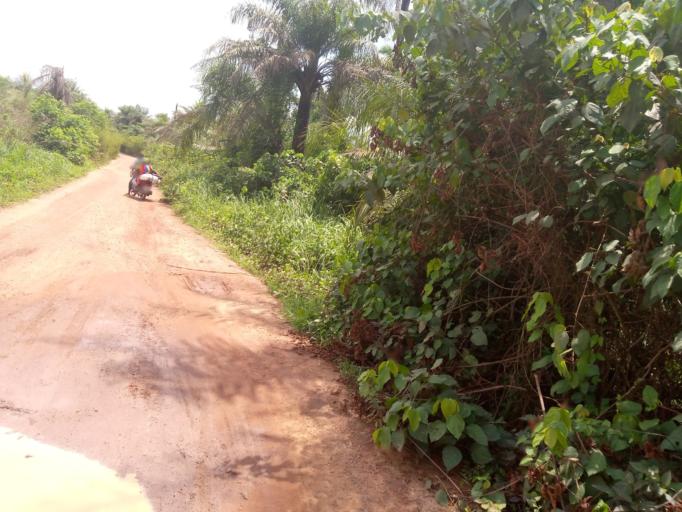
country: SL
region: Western Area
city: Waterloo
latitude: 8.3759
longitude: -12.9649
